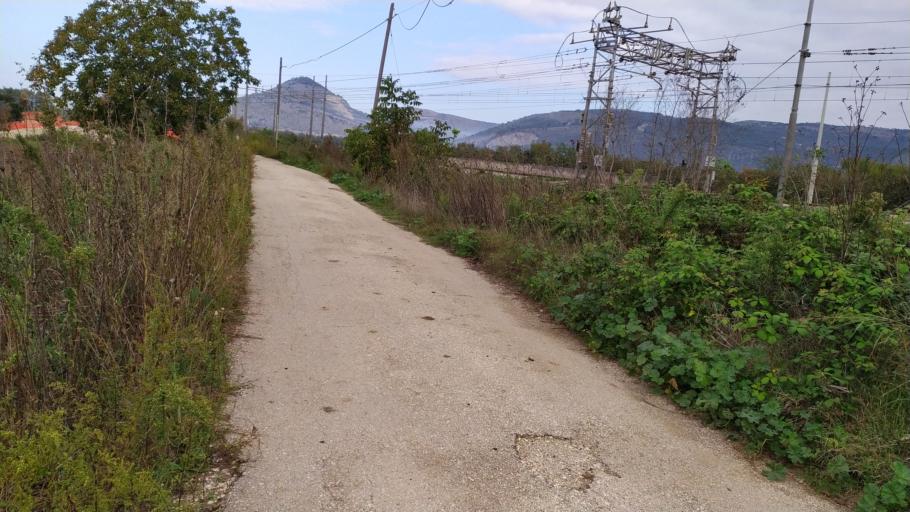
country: IT
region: Campania
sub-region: Provincia di Caserta
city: Montedecoro
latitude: 41.0184
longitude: 14.4050
